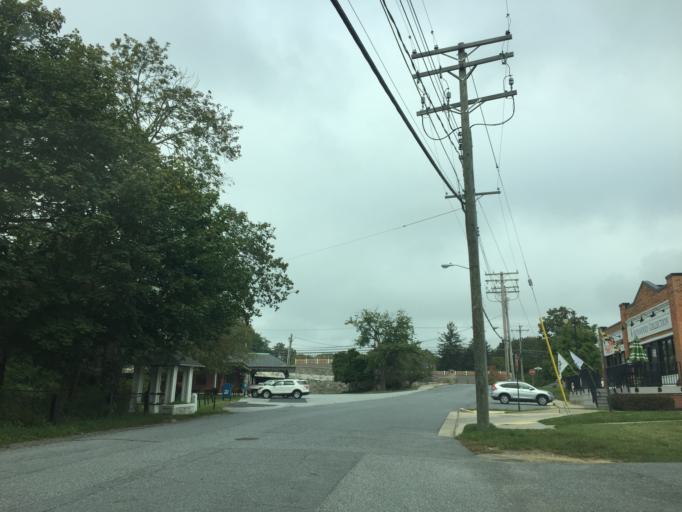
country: US
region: Maryland
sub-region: Baltimore County
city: Reisterstown
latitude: 39.4746
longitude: -76.8189
